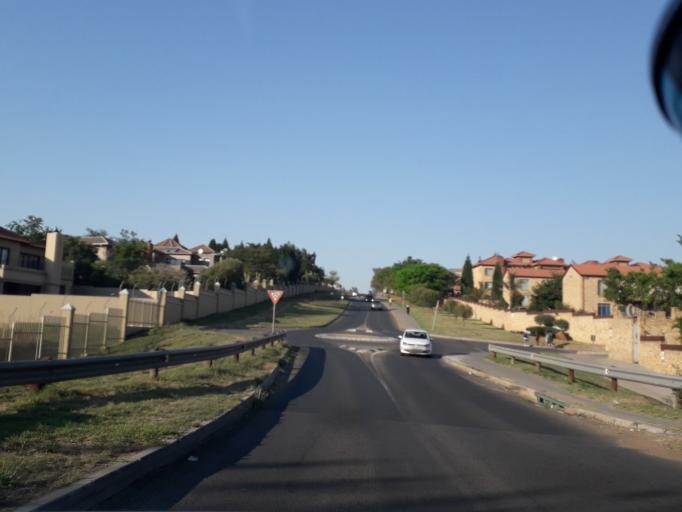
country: ZA
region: Gauteng
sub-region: City of Johannesburg Metropolitan Municipality
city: Roodepoort
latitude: -26.0856
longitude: 27.9077
